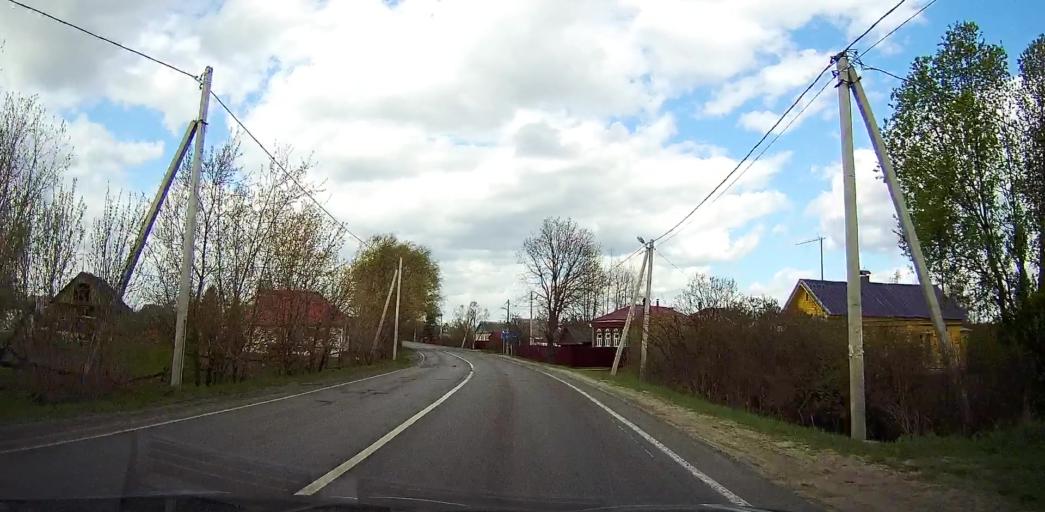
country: RU
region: Moskovskaya
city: Davydovo
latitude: 55.6340
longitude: 38.8691
